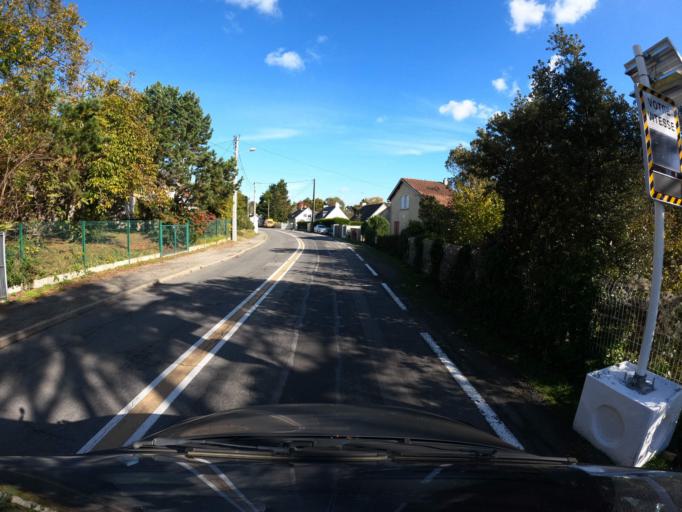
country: FR
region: Pays de la Loire
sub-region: Departement de la Loire-Atlantique
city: La Baule-Escoublac
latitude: 47.2894
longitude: -2.3661
